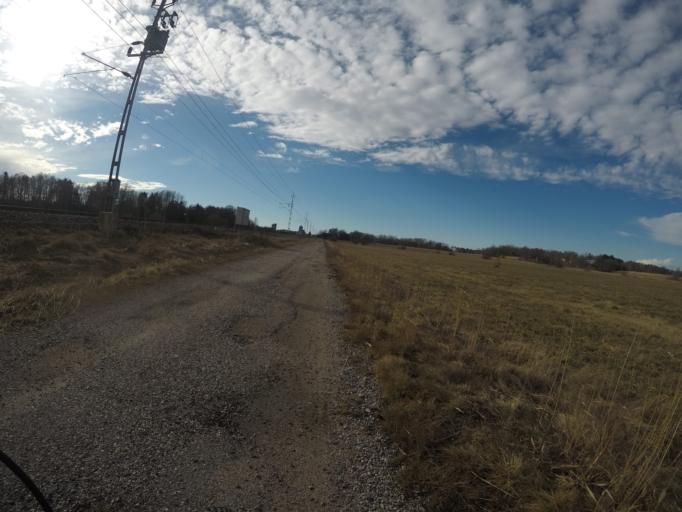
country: SE
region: Vaestmanland
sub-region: Kungsors Kommun
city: Kungsoer
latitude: 59.4242
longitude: 16.1492
